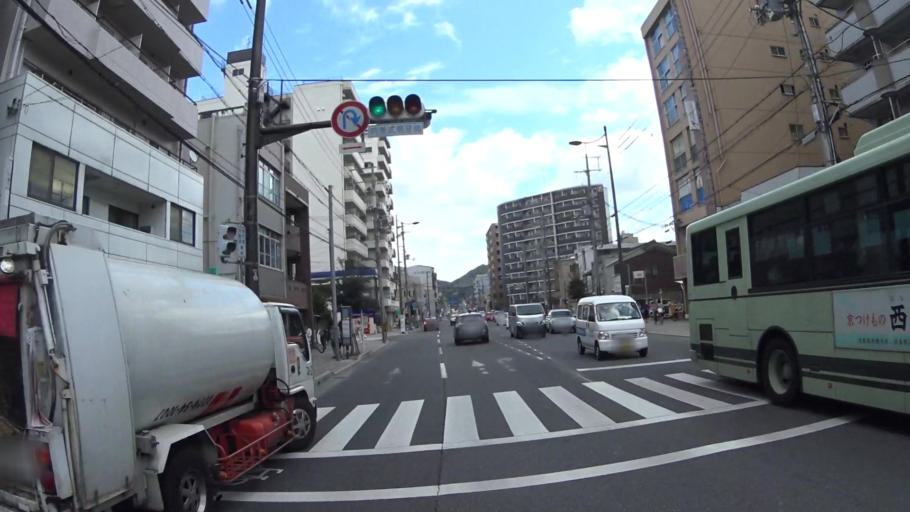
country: JP
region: Kyoto
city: Kyoto
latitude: 34.9893
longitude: 135.7627
